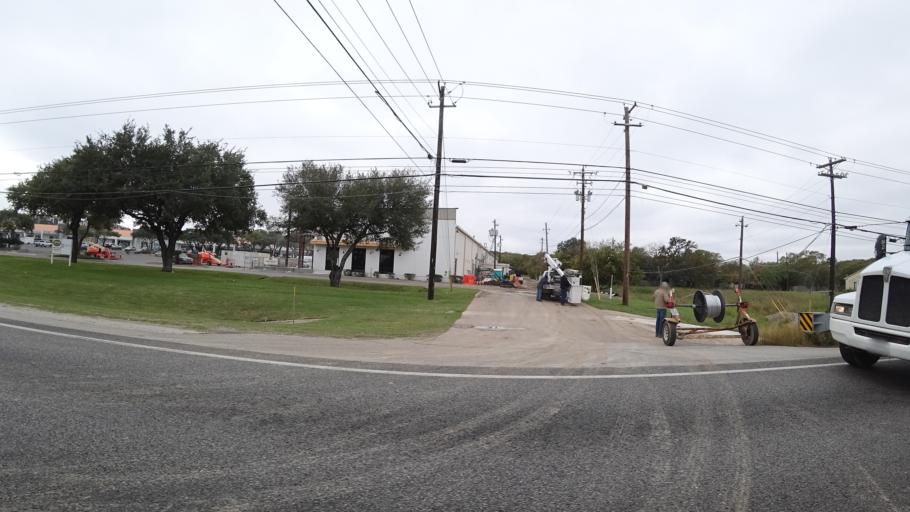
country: US
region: Texas
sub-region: Travis County
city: Barton Creek
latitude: 30.2359
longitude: -97.8775
